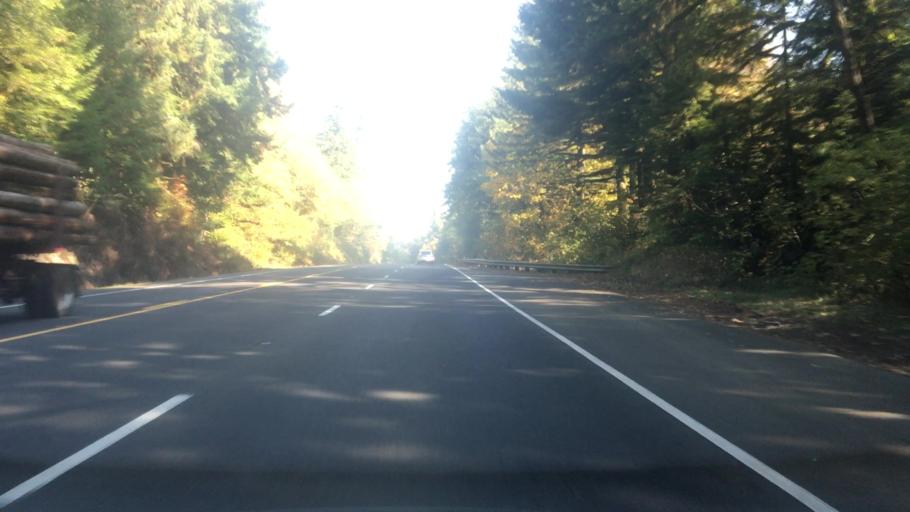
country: US
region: Oregon
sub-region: Lincoln County
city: Rose Lodge
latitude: 45.0485
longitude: -123.7902
